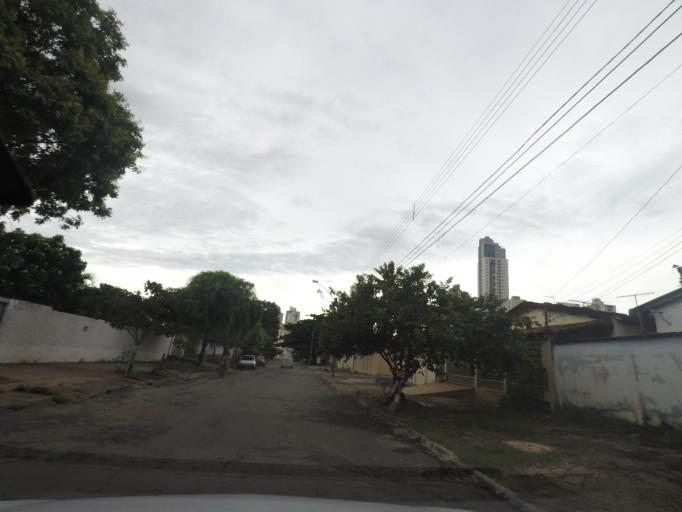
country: BR
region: Goias
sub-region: Goiania
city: Goiania
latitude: -16.7157
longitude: -49.2442
